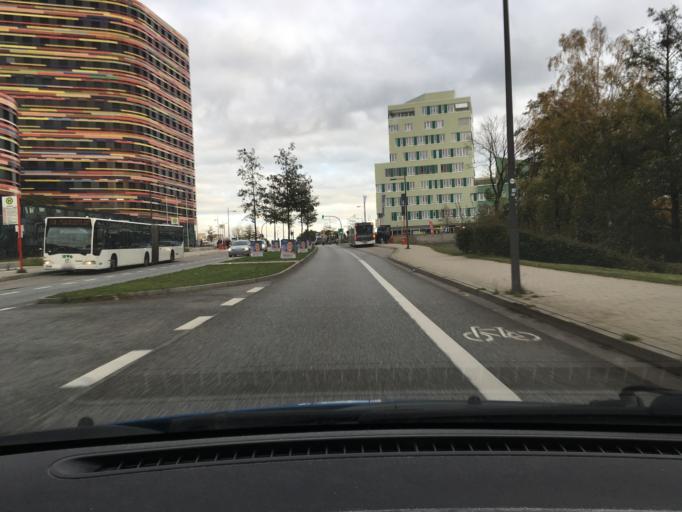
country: DE
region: Hamburg
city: Kleiner Grasbrook
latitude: 53.4978
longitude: 10.0021
